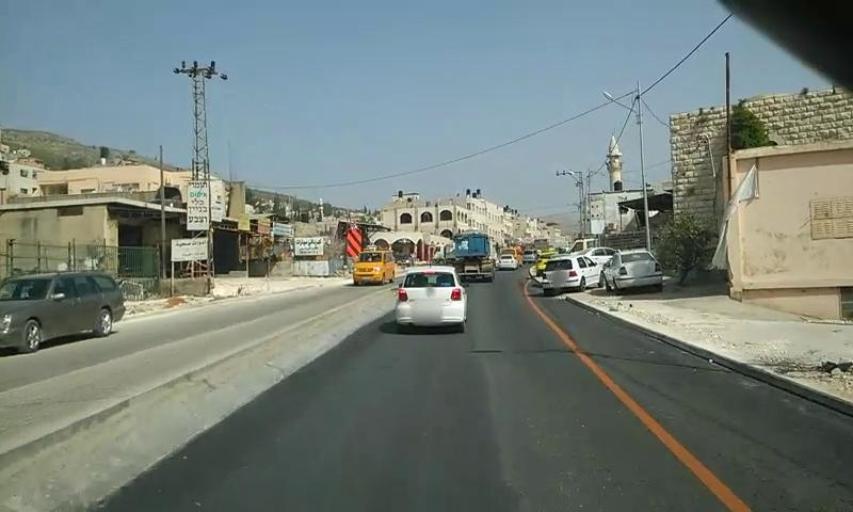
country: PS
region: West Bank
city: Huwwarah
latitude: 32.1482
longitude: 35.2578
